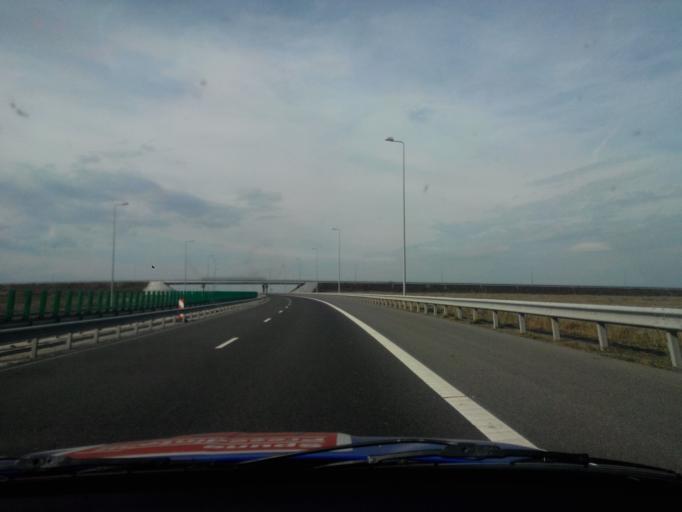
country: RO
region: Constanta
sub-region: Comuna Cumpana
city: Cumpana
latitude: 44.1443
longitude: 28.5576
